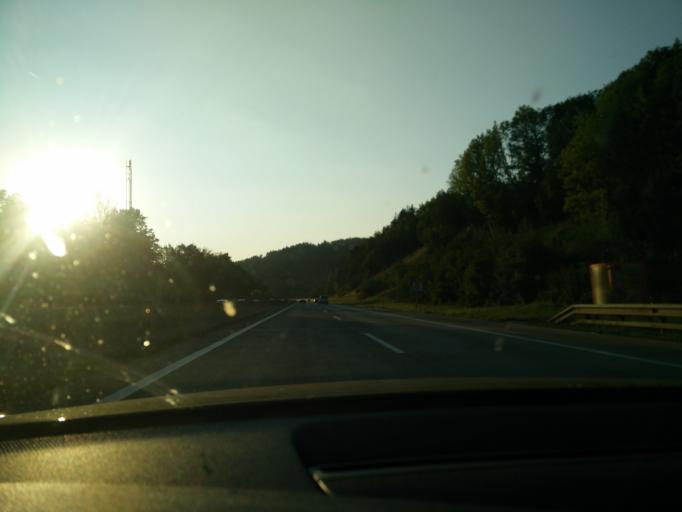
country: AT
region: Carinthia
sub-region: Politischer Bezirk Klagenfurt Land
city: Maria Worth
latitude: 46.6303
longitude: 14.1818
